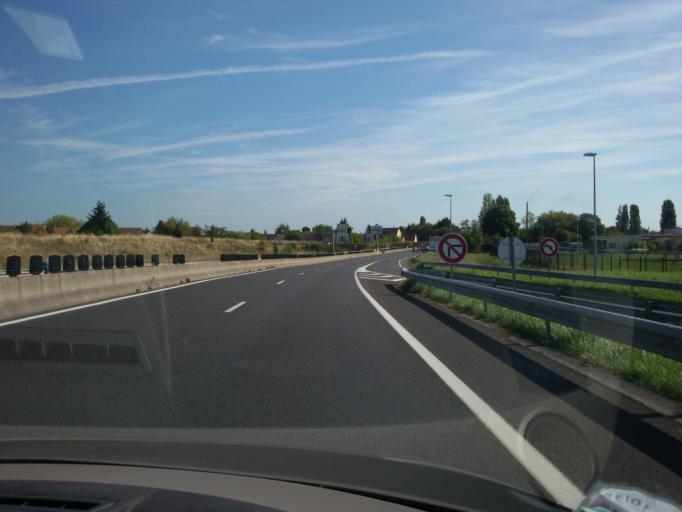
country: FR
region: Ile-de-France
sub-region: Departement de l'Essonne
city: Le Plessis-Pate
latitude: 48.6052
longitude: 2.3225
